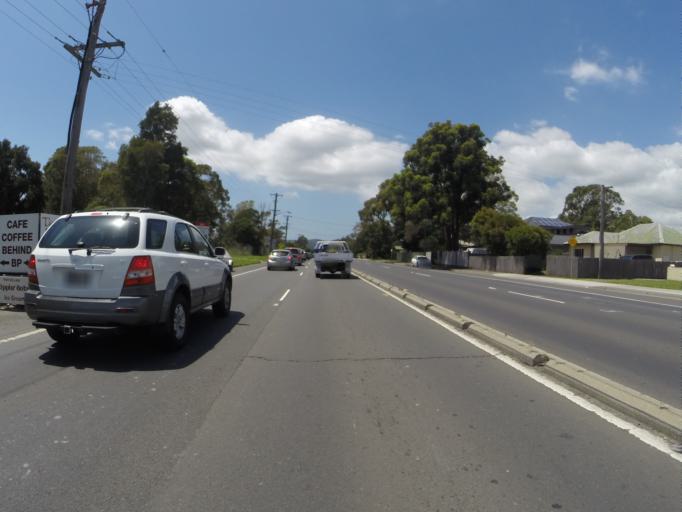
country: AU
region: New South Wales
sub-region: Shellharbour
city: Albion Park Rail
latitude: -34.5529
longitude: 150.7887
